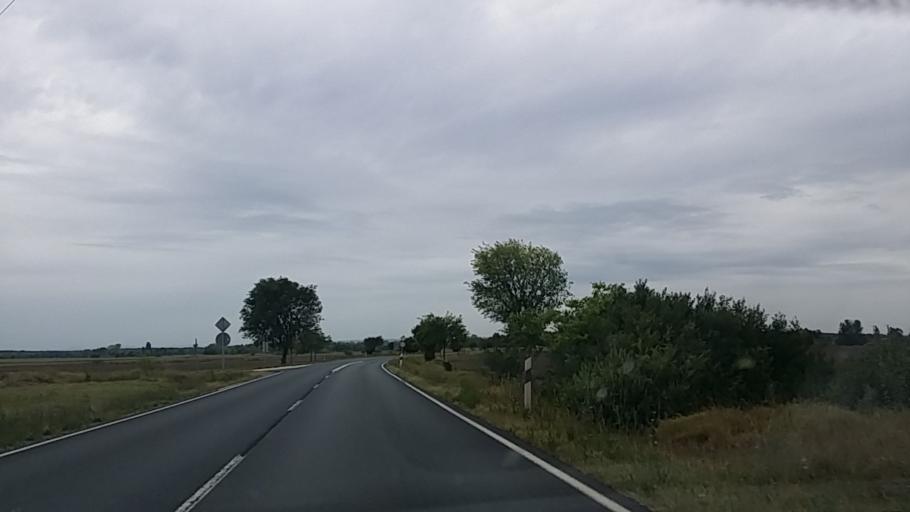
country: HU
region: Gyor-Moson-Sopron
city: Fertoszentmiklos
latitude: 47.5896
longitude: 16.8552
